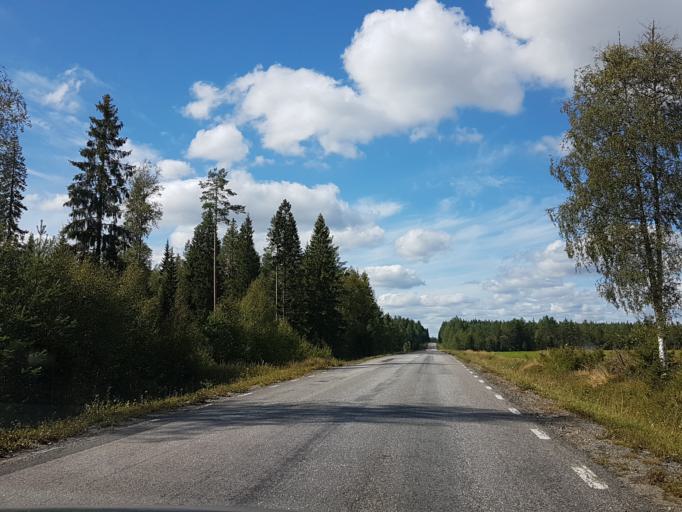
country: SE
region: Vaesterbotten
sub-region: Umea Kommun
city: Saevar
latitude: 64.2058
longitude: 20.4988
